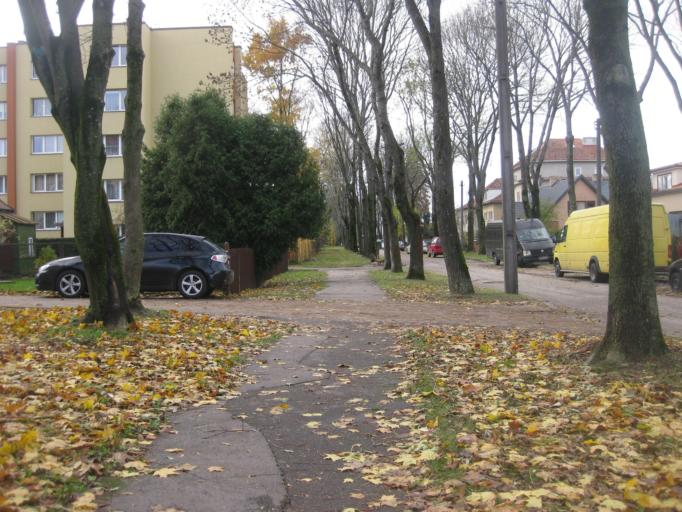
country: LT
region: Kauno apskritis
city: Dainava (Kaunas)
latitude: 54.9058
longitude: 23.9464
